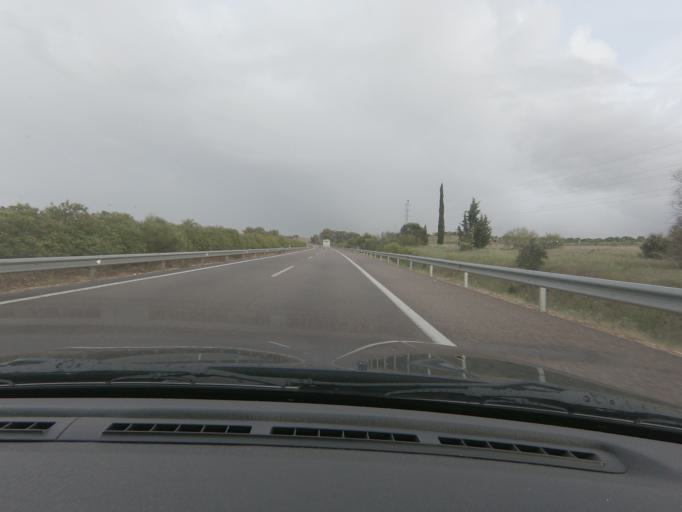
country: ES
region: Extremadura
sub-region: Provincia de Badajoz
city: Badajoz
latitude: 38.8754
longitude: -6.8794
